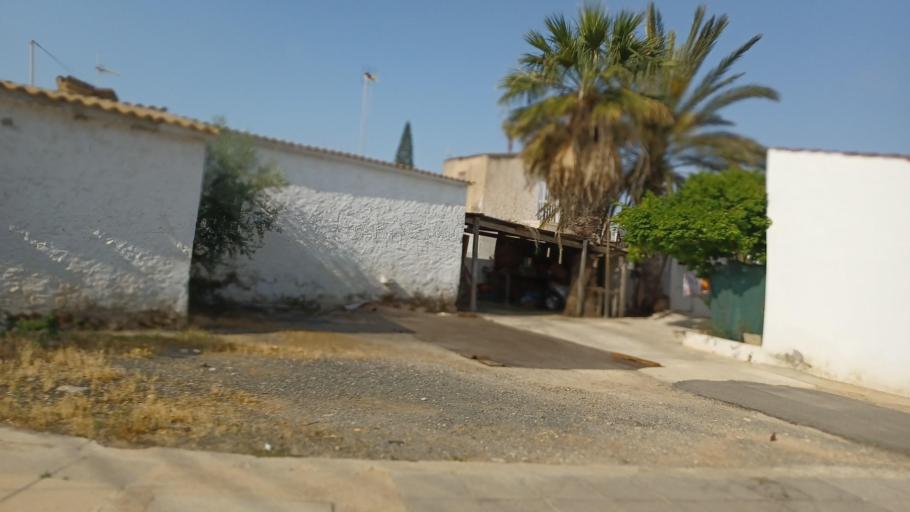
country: CY
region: Ammochostos
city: Avgorou
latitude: 35.0392
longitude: 33.8386
